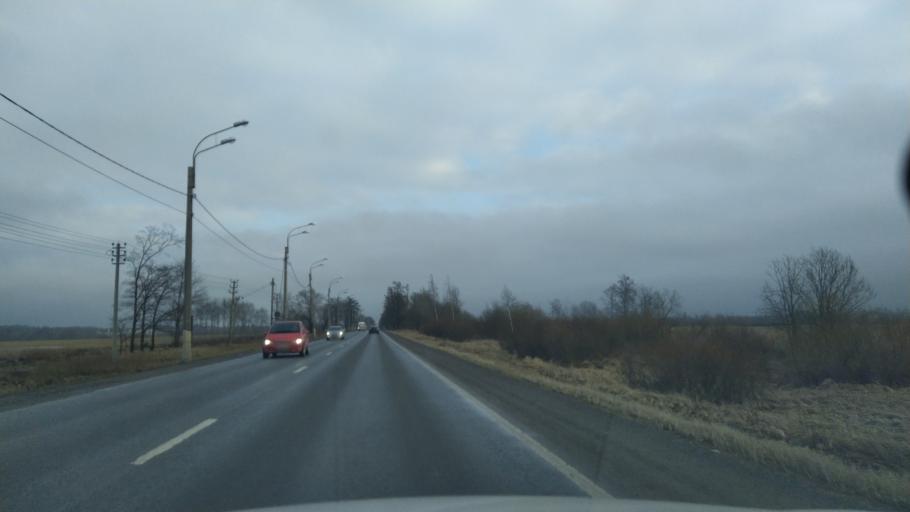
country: RU
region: St.-Petersburg
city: Aleksandrovskaya
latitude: 59.7108
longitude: 30.3167
